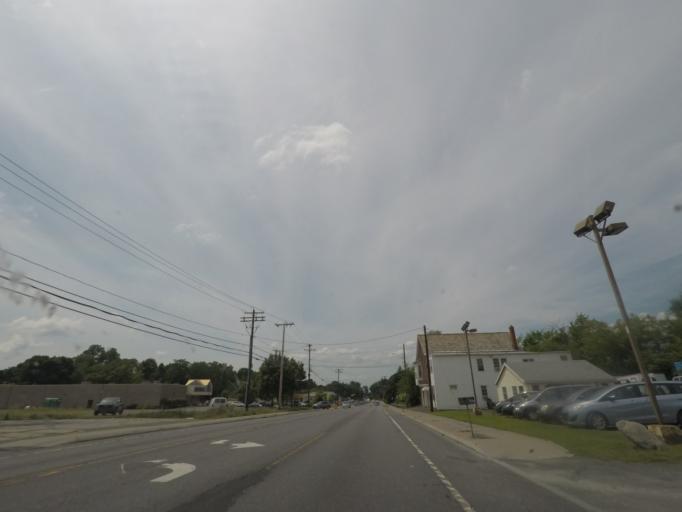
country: US
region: New York
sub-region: Albany County
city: Green Island
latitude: 42.7425
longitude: -73.6498
